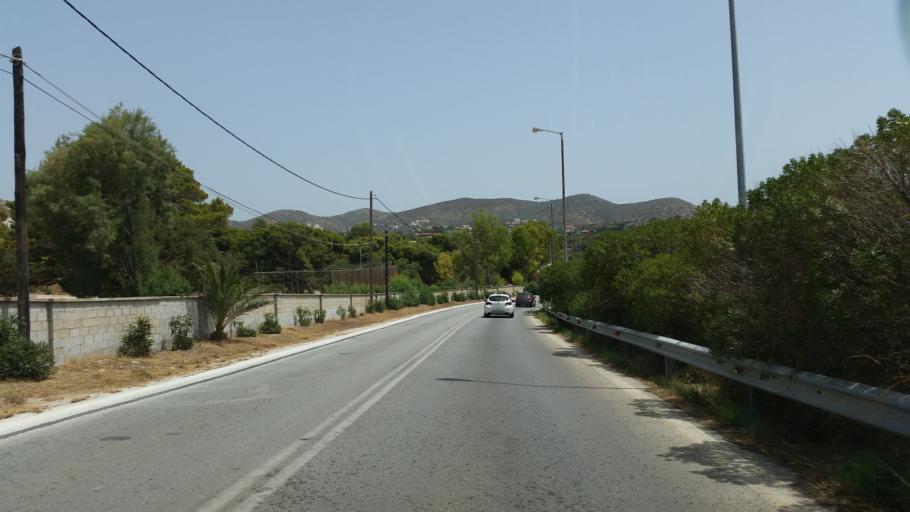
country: GR
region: Attica
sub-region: Nomarchia Anatolikis Attikis
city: Palaia Fokaia
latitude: 37.7050
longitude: 23.9391
